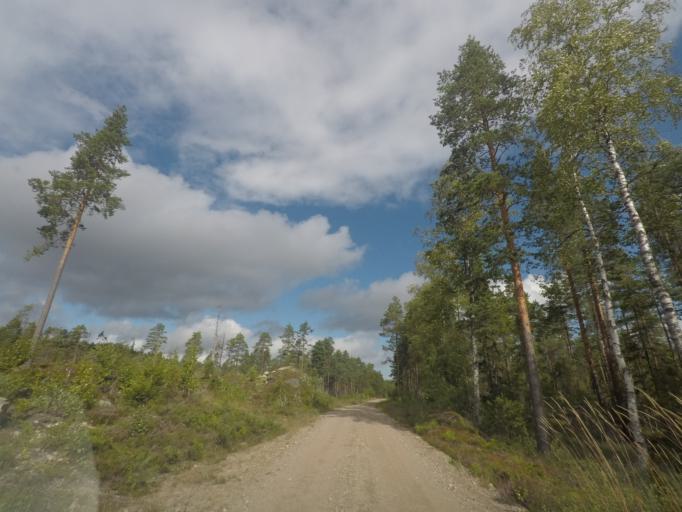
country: SE
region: Vaermland
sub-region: Filipstads Kommun
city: Lesjofors
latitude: 60.0547
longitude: 14.4419
